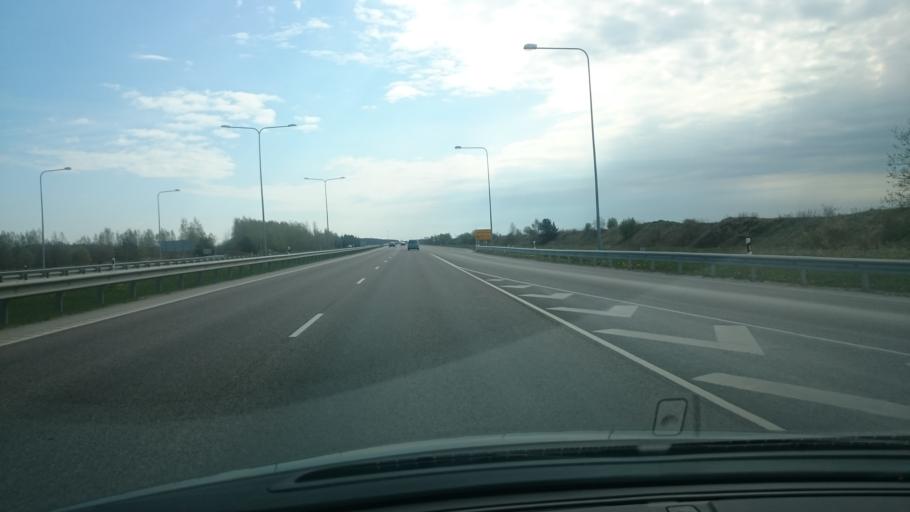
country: EE
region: Harju
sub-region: Maardu linn
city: Maardu
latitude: 59.4517
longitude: 25.0348
